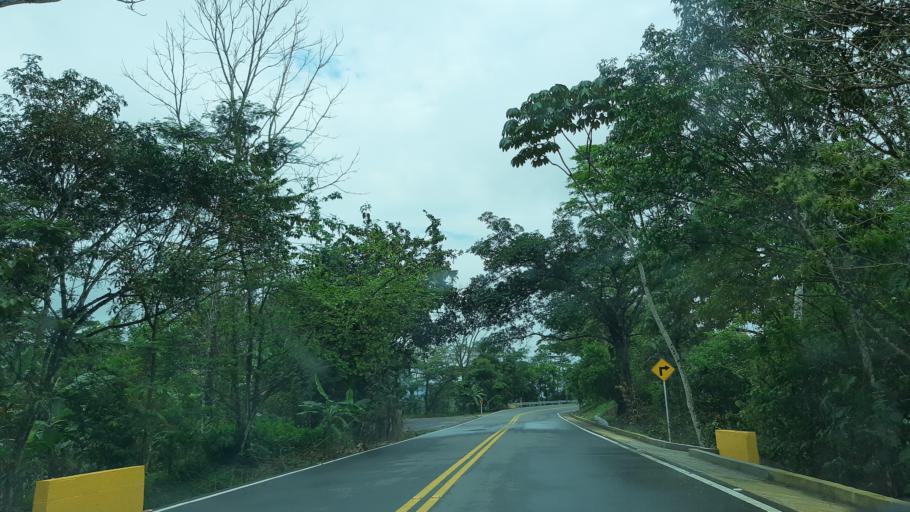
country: CO
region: Casanare
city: Sabanalarga
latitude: 4.7736
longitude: -73.0383
